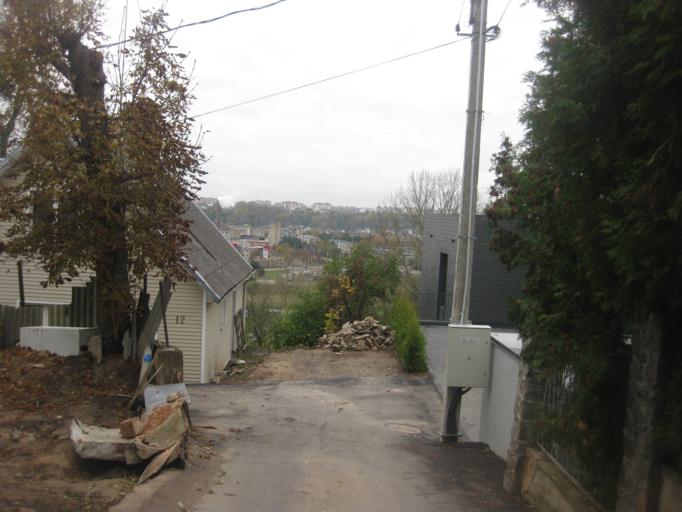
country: LT
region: Kauno apskritis
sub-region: Kaunas
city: Kaunas
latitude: 54.9118
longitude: 23.9137
